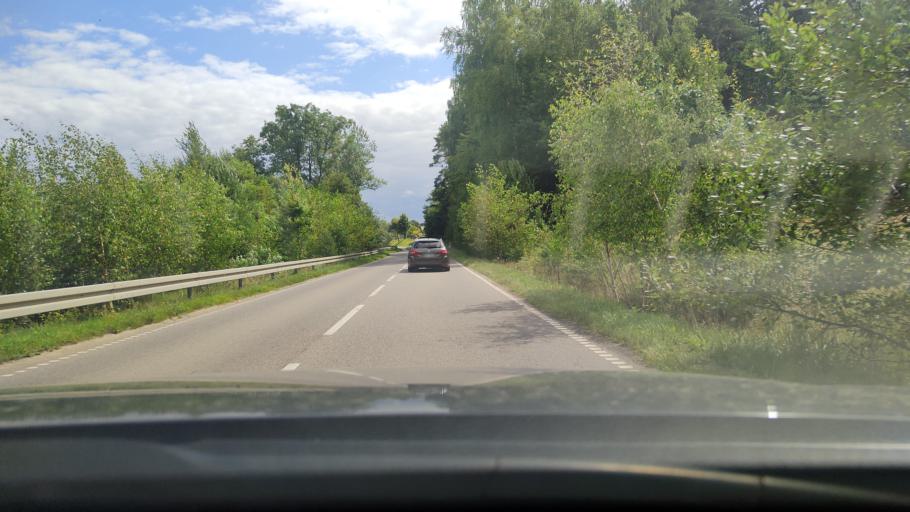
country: PL
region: Pomeranian Voivodeship
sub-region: Powiat wejherowski
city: Wejherowo
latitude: 54.5466
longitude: 18.2831
